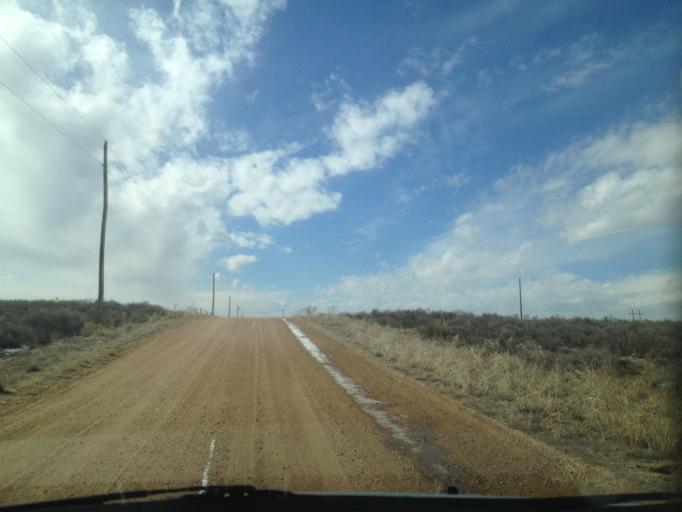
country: US
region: Colorado
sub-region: Weld County
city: Keenesburg
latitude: 40.2820
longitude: -104.2578
